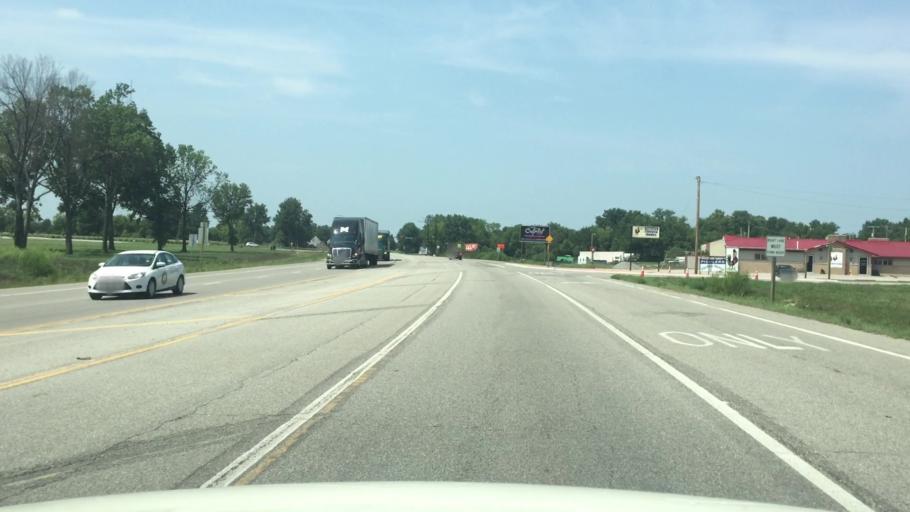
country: US
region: Kansas
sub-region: Crawford County
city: Pittsburg
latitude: 37.3427
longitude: -94.7058
